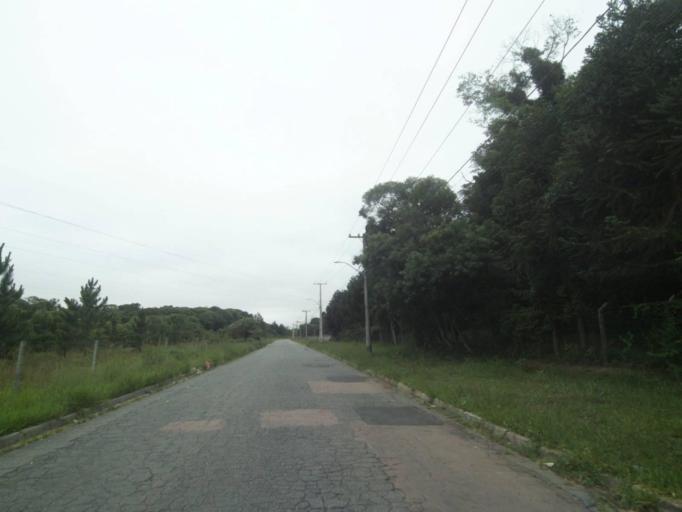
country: BR
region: Parana
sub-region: Araucaria
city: Araucaria
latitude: -25.5419
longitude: -49.3210
